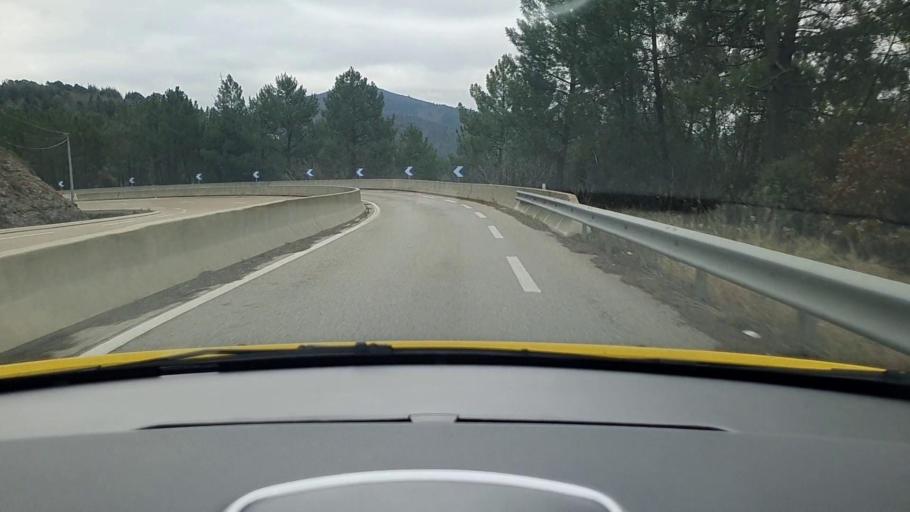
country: FR
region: Languedoc-Roussillon
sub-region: Departement du Gard
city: Les Salles-du-Gardon
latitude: 44.2585
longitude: 4.0408
